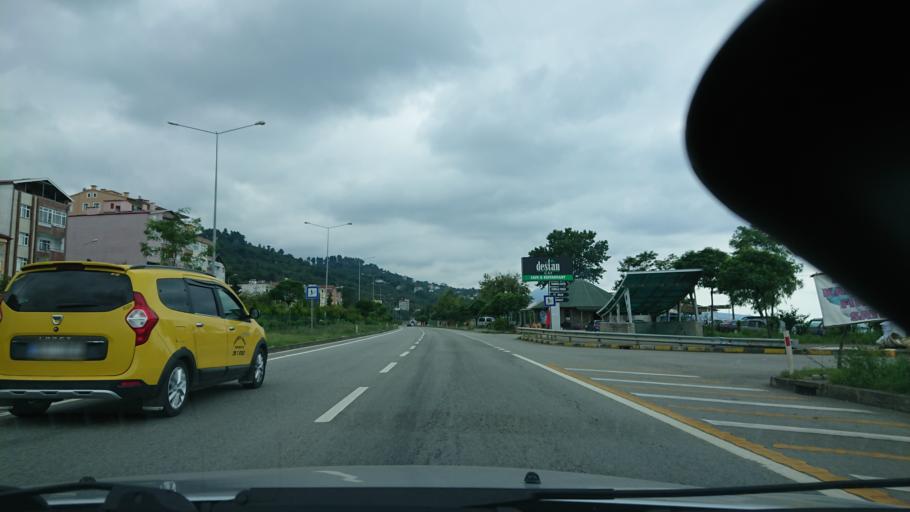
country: TR
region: Giresun
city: Gorele
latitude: 41.0405
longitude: 39.0653
